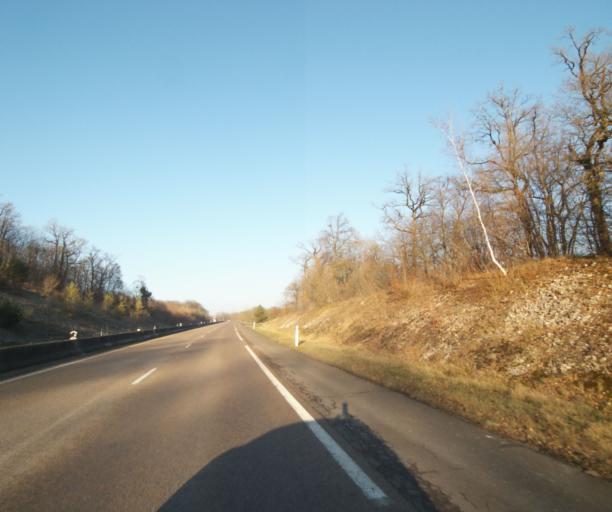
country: FR
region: Champagne-Ardenne
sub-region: Departement de la Haute-Marne
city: Chevillon
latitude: 48.5250
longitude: 5.0895
